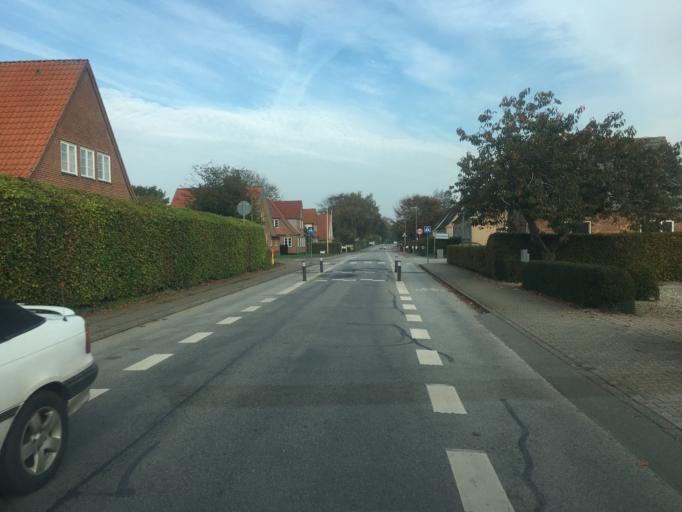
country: DK
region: South Denmark
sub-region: Tonder Kommune
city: Logumkloster
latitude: 55.0594
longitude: 8.9553
